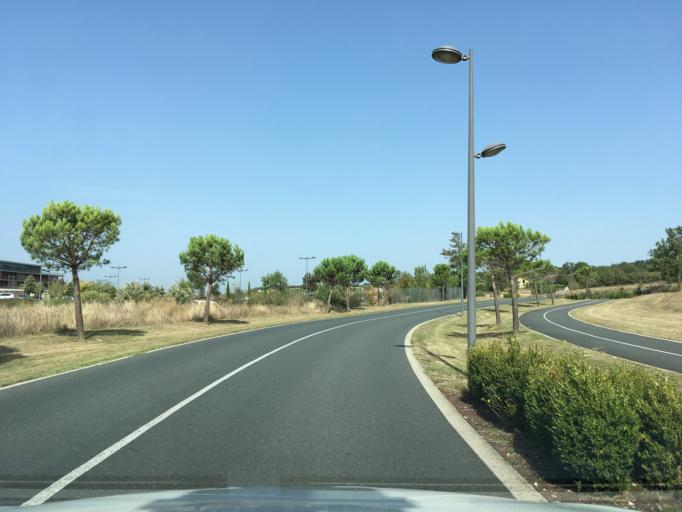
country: FR
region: Midi-Pyrenees
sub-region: Departement du Tarn
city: Lagarrigue
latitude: 43.5651
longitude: 2.2657
